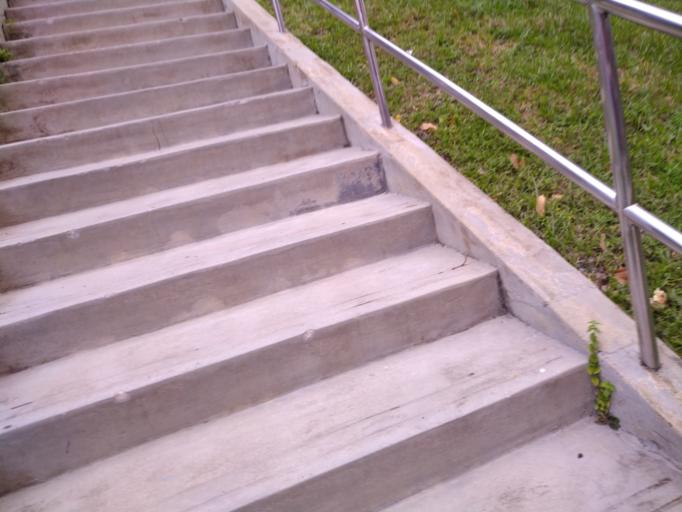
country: SG
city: Singapore
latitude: 1.2861
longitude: 103.8193
